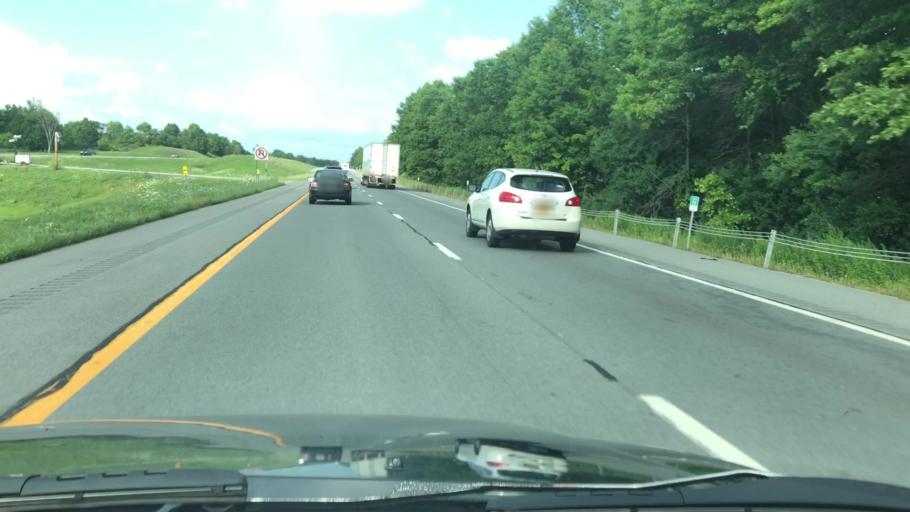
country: US
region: New York
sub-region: Orange County
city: Montgomery
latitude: 41.4917
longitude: -74.2711
